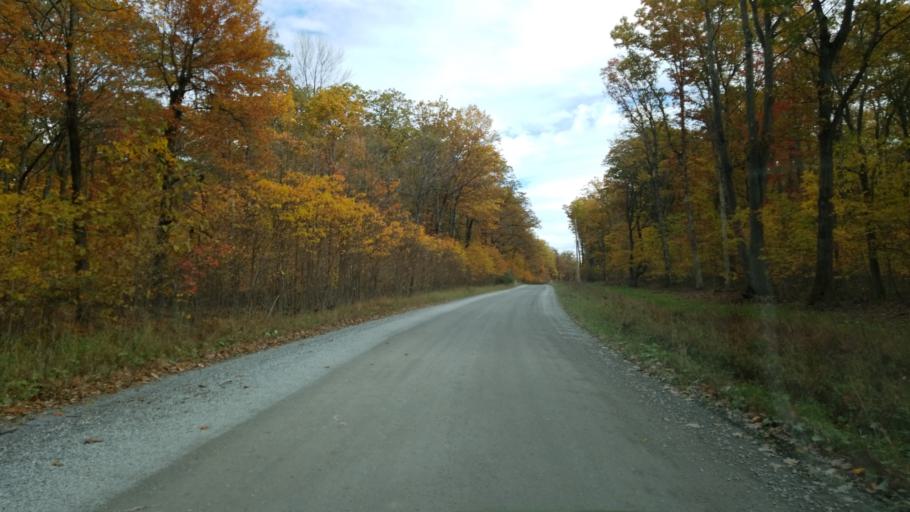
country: US
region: Pennsylvania
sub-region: Clearfield County
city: Clearfield
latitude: 41.1426
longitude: -78.4990
